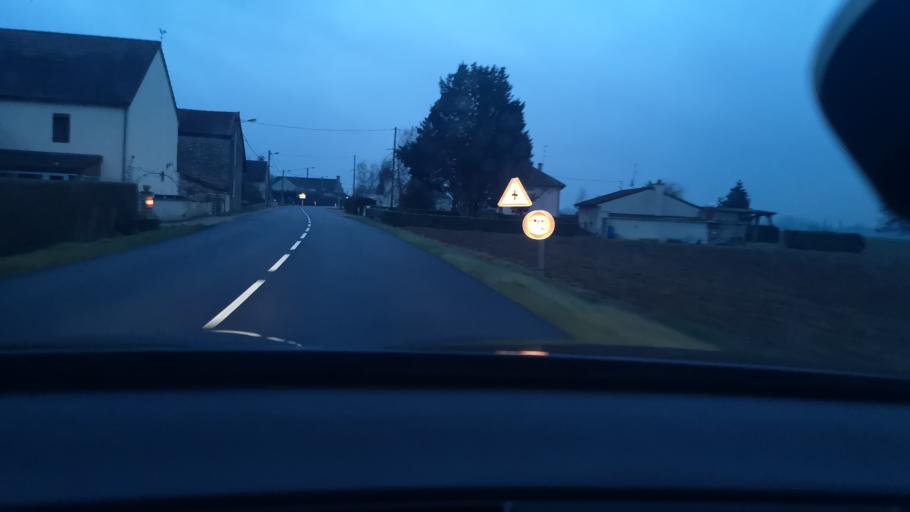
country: FR
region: Bourgogne
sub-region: Departement de Saone-et-Loire
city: Demigny
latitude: 46.9381
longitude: 4.8616
